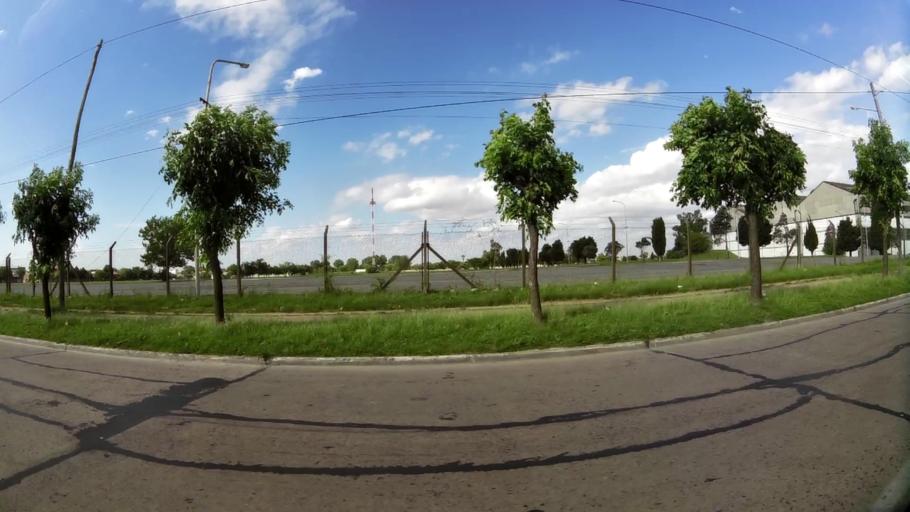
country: AR
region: Buenos Aires
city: San Justo
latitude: -34.6663
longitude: -58.5703
